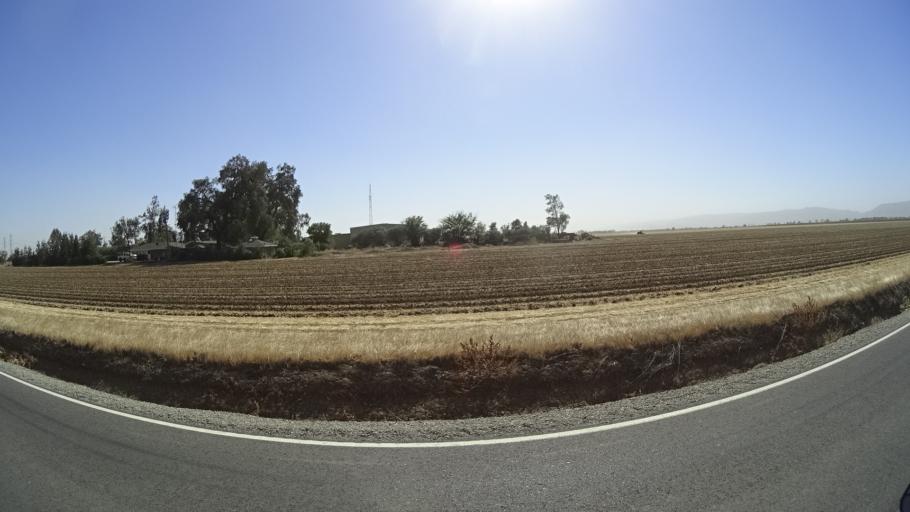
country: US
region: California
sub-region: Yolo County
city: Winters
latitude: 38.5840
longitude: -121.9351
